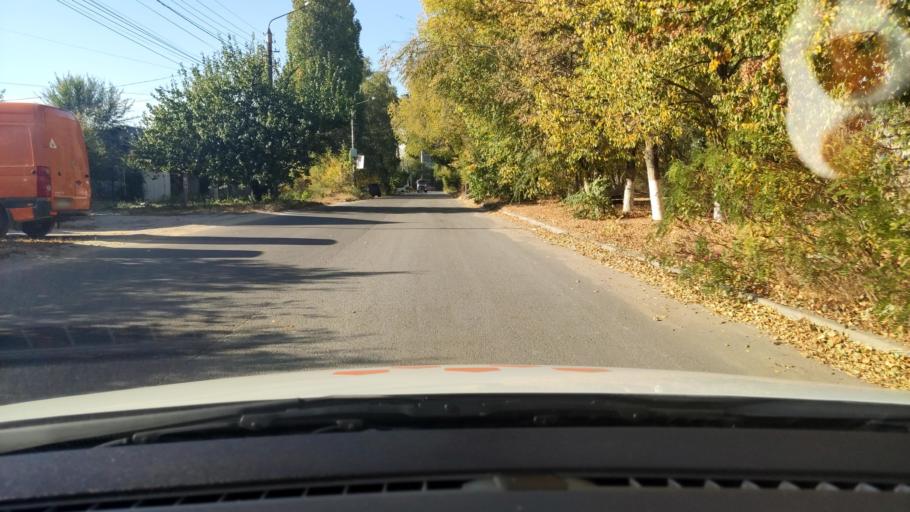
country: RU
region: Voronezj
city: Voronezh
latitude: 51.6823
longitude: 39.1461
